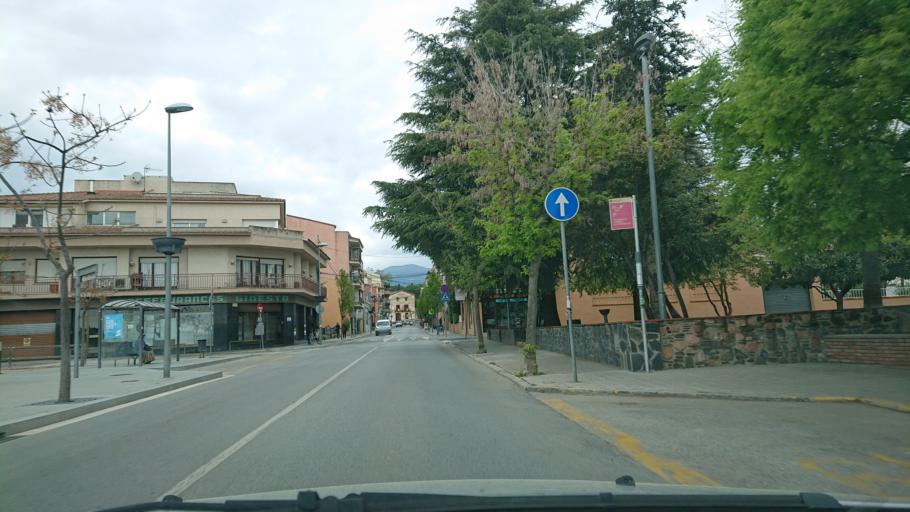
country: ES
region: Catalonia
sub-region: Provincia de Barcelona
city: Sant Pere de Vilamajor
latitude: 41.6717
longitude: 2.4021
